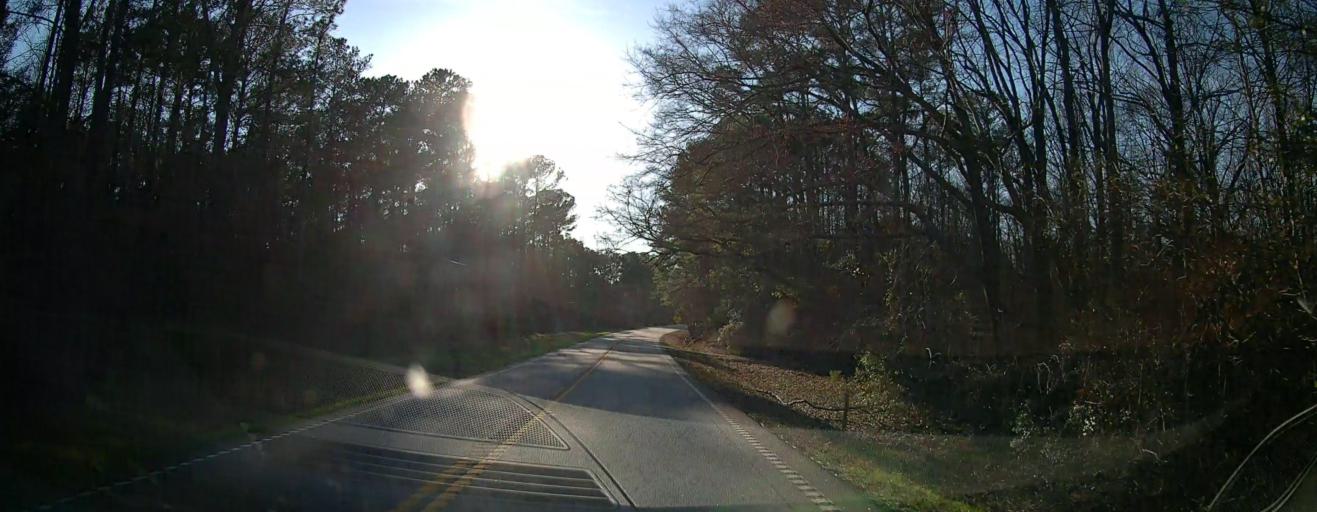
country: US
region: Alabama
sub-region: Chambers County
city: Valley
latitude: 32.7416
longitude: -85.0594
